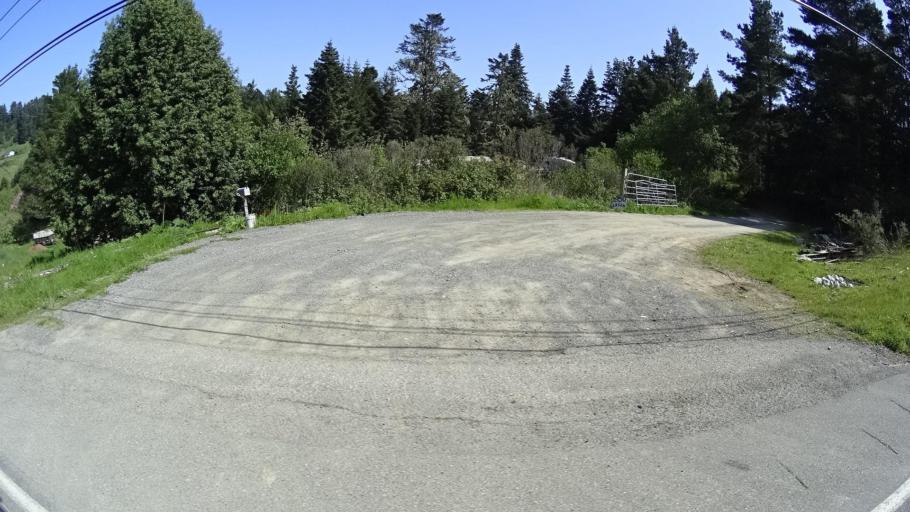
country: US
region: California
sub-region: Humboldt County
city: Hydesville
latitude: 40.5541
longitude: -124.1102
